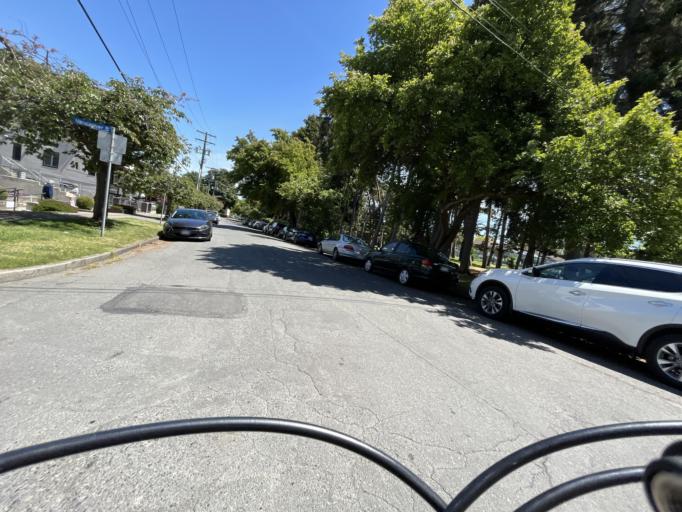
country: CA
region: British Columbia
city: Victoria
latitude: 48.4128
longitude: -123.3594
